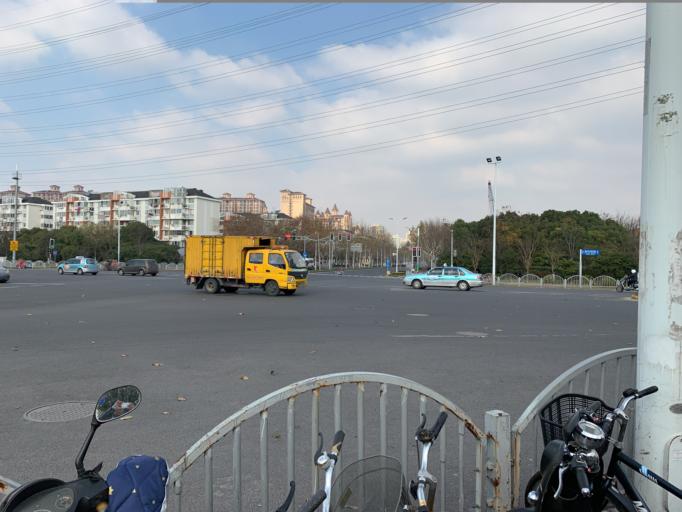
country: CN
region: Shanghai Shi
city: Huamu
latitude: 31.1895
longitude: 121.5363
